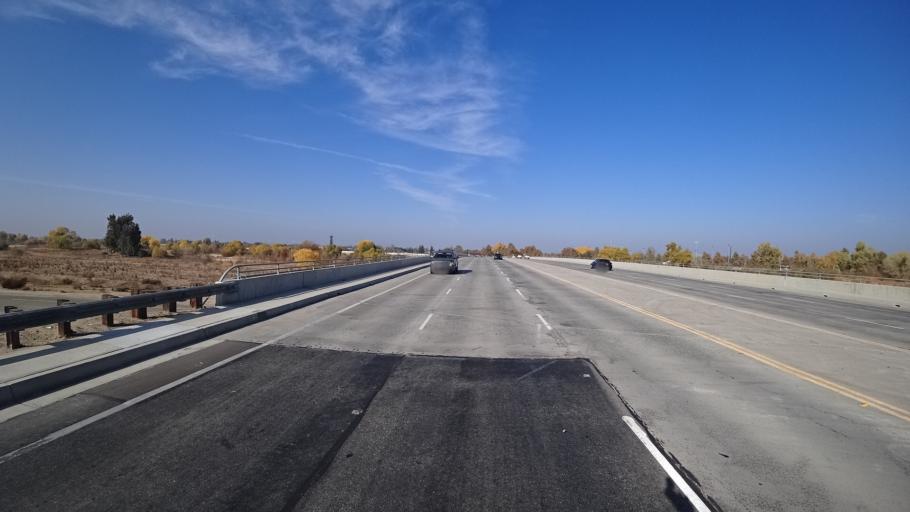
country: US
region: California
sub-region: Kern County
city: Rosedale
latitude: 35.3510
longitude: -119.1315
